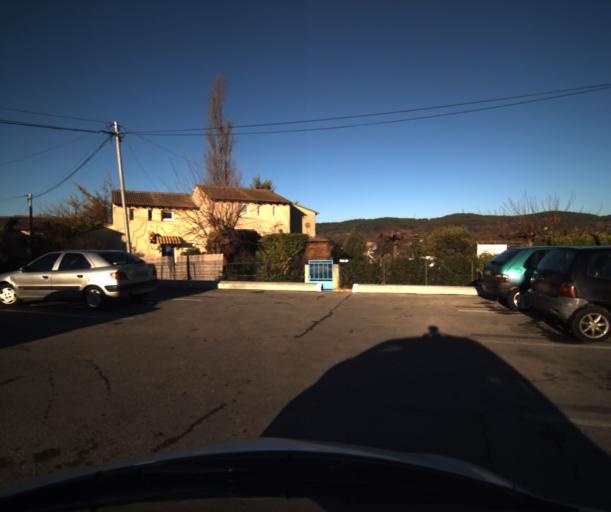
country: FR
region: Provence-Alpes-Cote d'Azur
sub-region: Departement du Vaucluse
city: Pertuis
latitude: 43.7024
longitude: 5.4936
